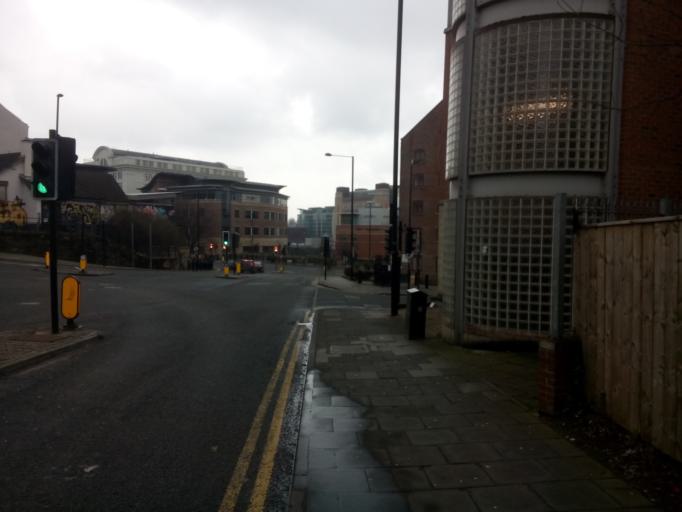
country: GB
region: England
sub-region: Gateshead
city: Gateshead
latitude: 54.9708
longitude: -1.6031
